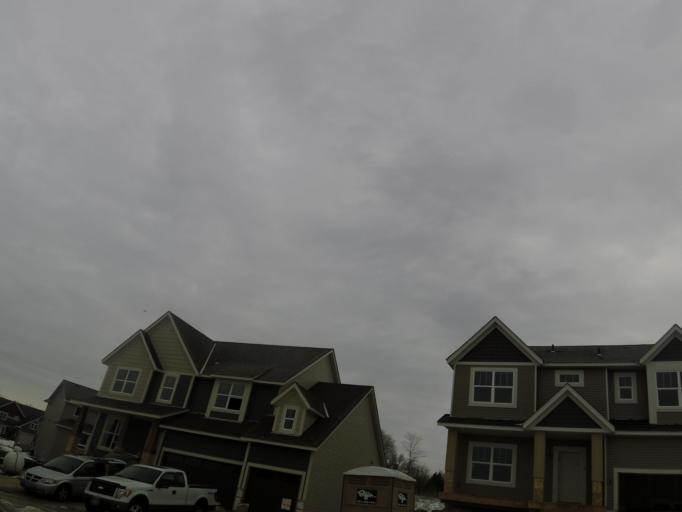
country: US
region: Minnesota
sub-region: Scott County
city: Savage
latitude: 44.7695
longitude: -93.3273
